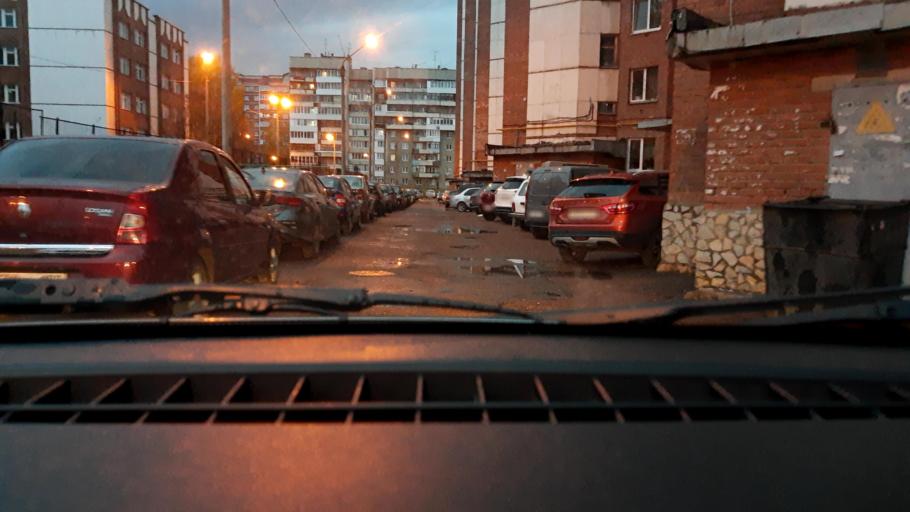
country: RU
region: Bashkortostan
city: Ufa
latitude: 54.8193
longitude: 56.1216
